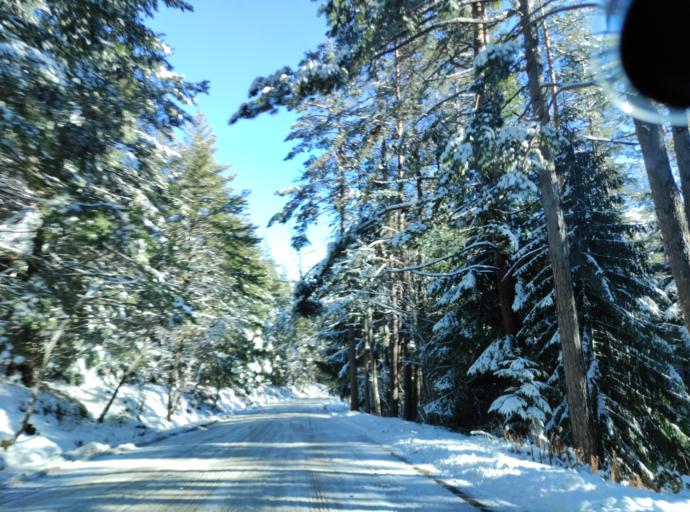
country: BG
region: Sofia-Capital
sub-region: Stolichna Obshtina
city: Sofia
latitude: 42.5886
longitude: 23.3019
